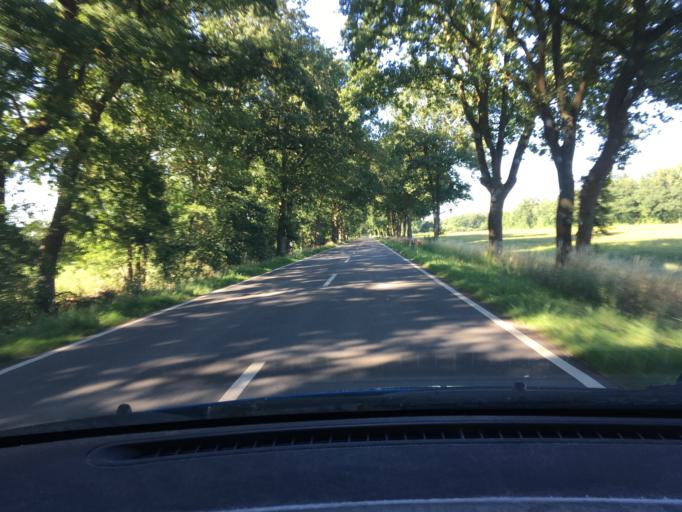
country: DE
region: Mecklenburg-Vorpommern
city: Boizenburg
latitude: 53.3303
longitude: 10.6791
